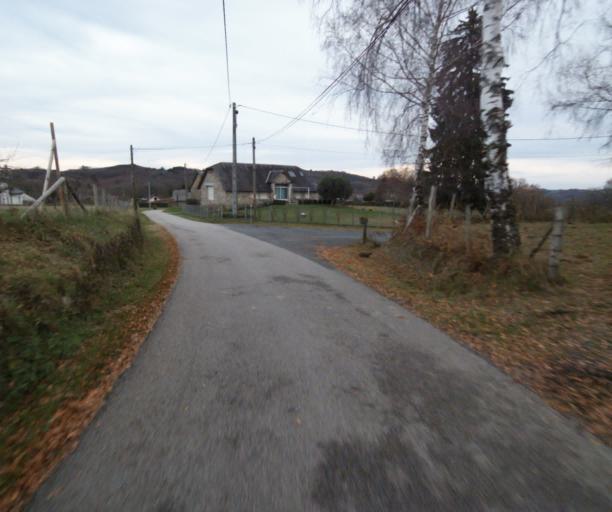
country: FR
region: Limousin
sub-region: Departement de la Correze
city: Saint-Mexant
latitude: 45.2526
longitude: 1.6589
